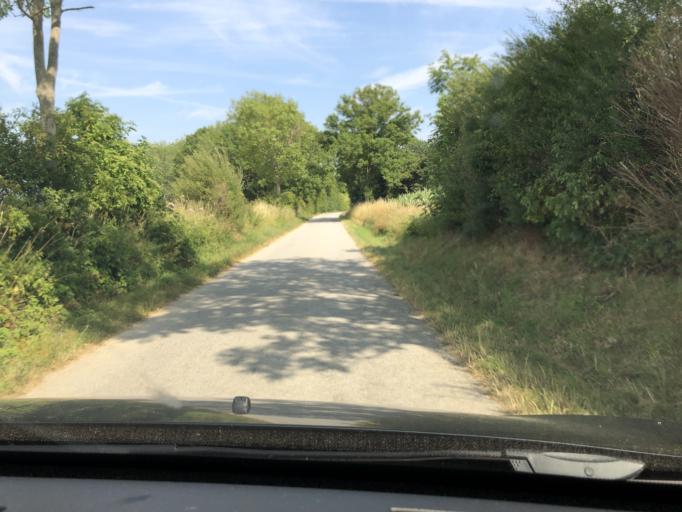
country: DK
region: South Denmark
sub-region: AEro Kommune
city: AEroskobing
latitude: 54.9146
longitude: 10.3111
